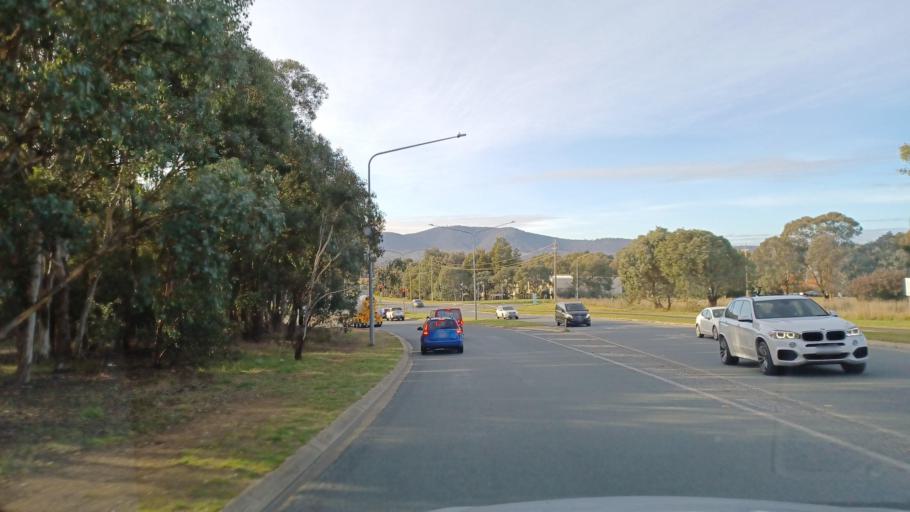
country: AU
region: Australian Capital Territory
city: Kaleen
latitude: -35.2198
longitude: 149.1352
